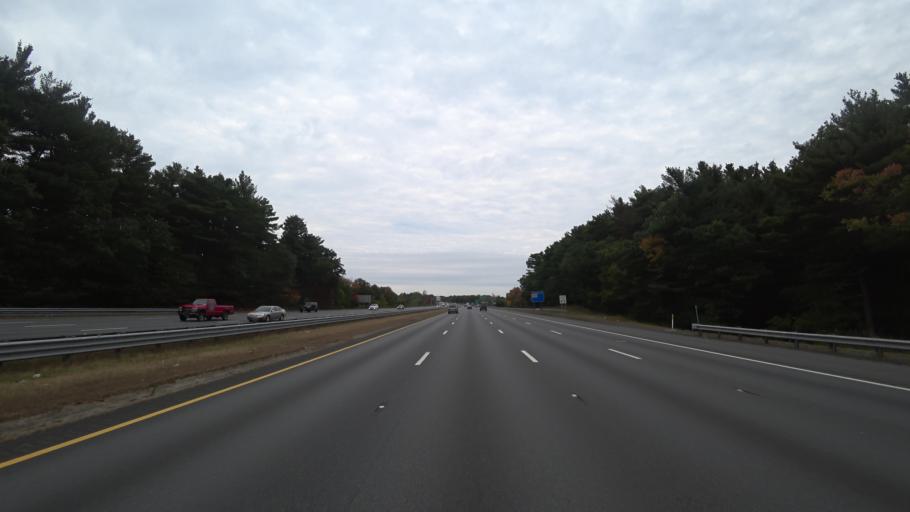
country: US
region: Massachusetts
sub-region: Middlesex County
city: Wilmington
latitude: 42.5473
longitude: -71.1360
